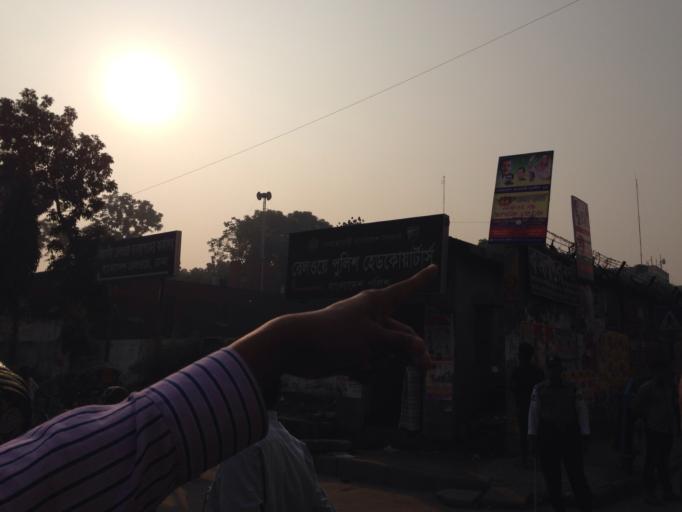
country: BD
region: Dhaka
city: Paltan
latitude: 23.7315
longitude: 90.4253
